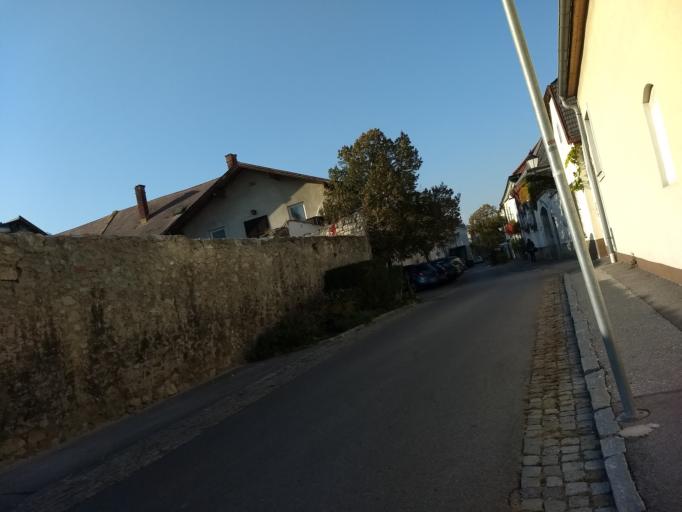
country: AT
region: Lower Austria
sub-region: Politischer Bezirk Modling
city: Perchtoldsdorf
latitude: 48.1180
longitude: 16.2671
